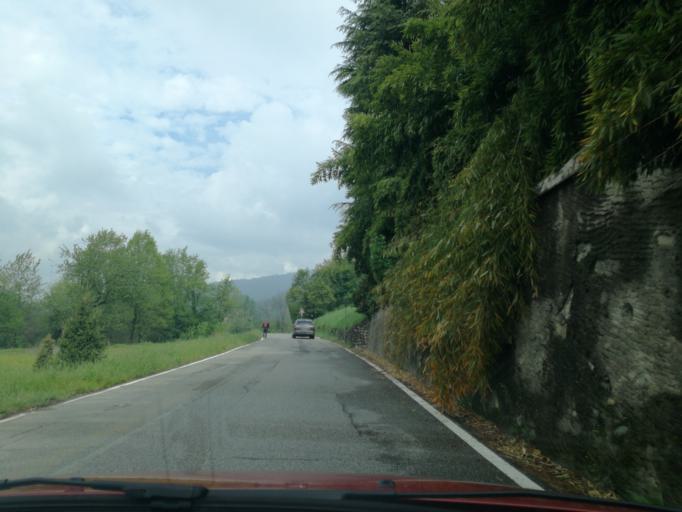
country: IT
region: Lombardy
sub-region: Provincia di Lecco
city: Canova-San Zeno
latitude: 45.7256
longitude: 9.3924
